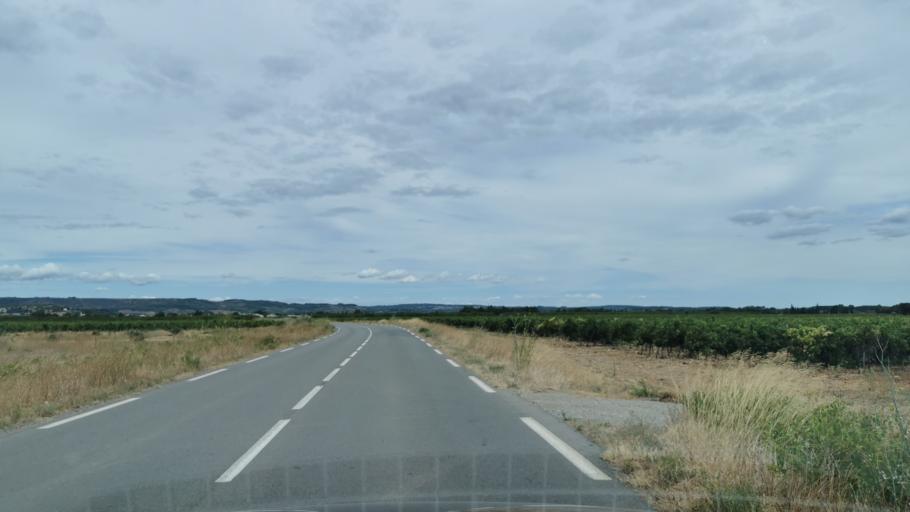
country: FR
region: Languedoc-Roussillon
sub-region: Departement de l'Aude
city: Argeliers
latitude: 43.2932
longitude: 2.9031
